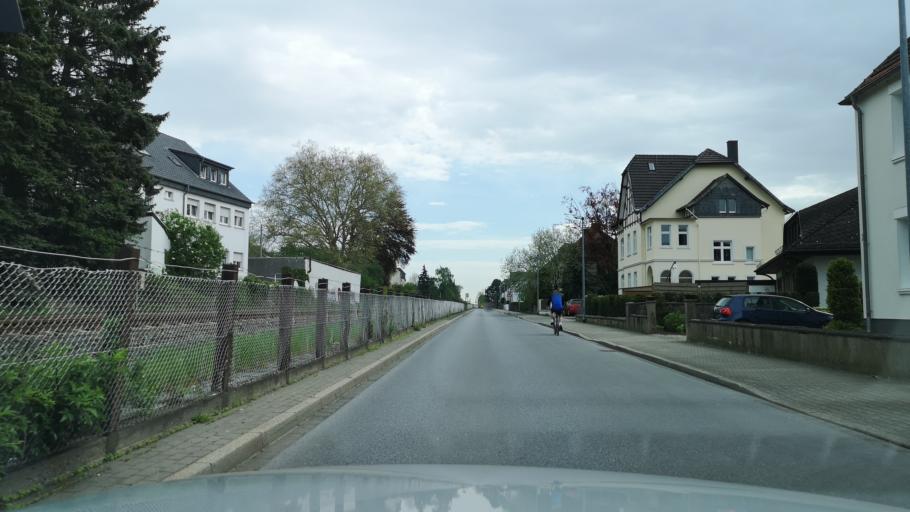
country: DE
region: North Rhine-Westphalia
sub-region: Regierungsbezirk Arnsberg
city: Frondenberg
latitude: 51.4726
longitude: 7.7725
